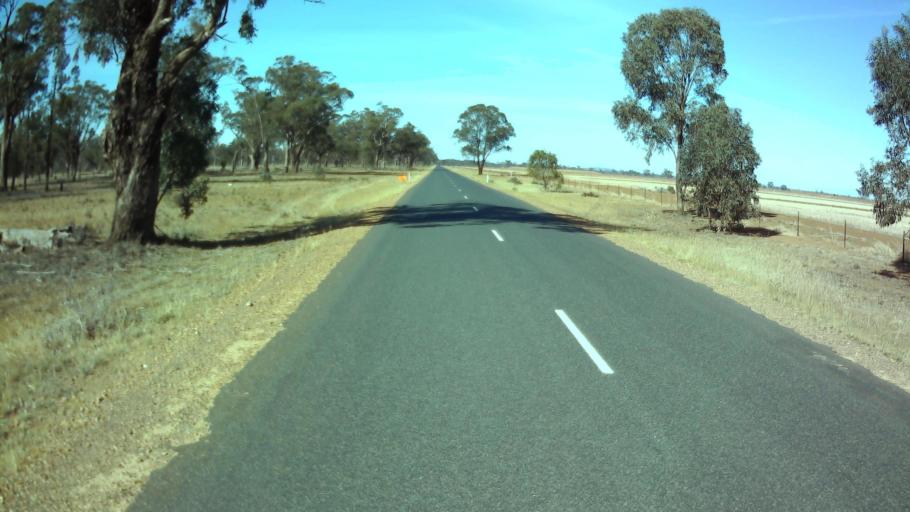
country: AU
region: New South Wales
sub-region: Weddin
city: Grenfell
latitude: -34.1189
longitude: 147.8145
